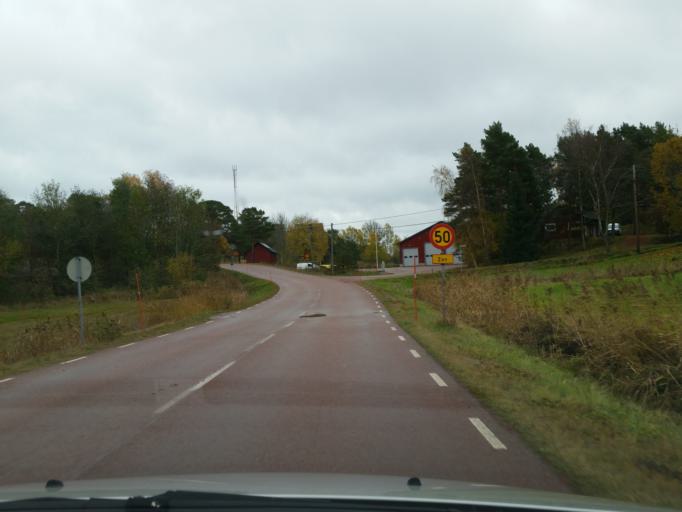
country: AX
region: Alands landsbygd
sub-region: Lumparland
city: Lumparland
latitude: 60.1180
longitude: 20.2537
